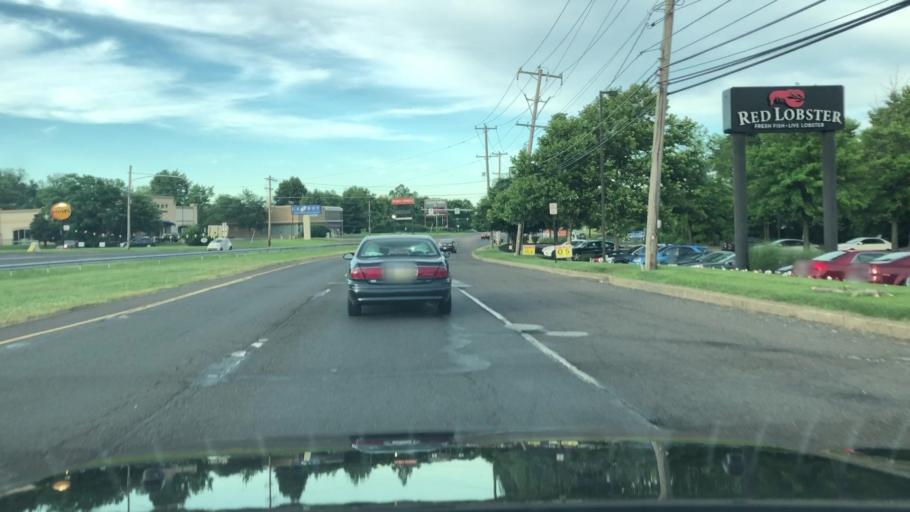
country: US
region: Pennsylvania
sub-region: Bucks County
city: Woodbourne
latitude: 40.1784
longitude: -74.8807
